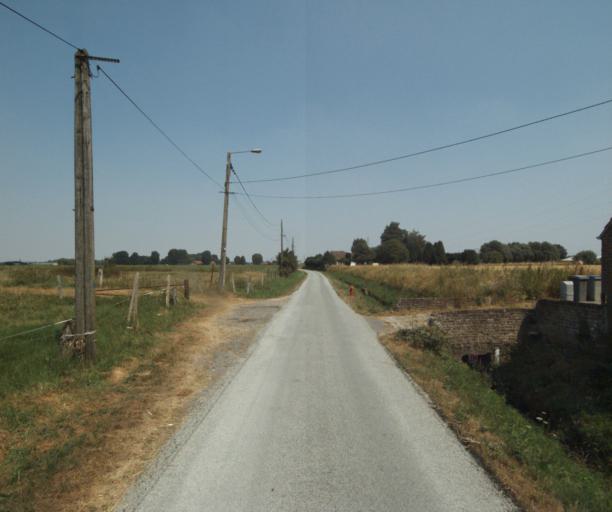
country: FR
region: Nord-Pas-de-Calais
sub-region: Departement du Nord
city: Wambrechies
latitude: 50.7077
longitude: 3.0494
